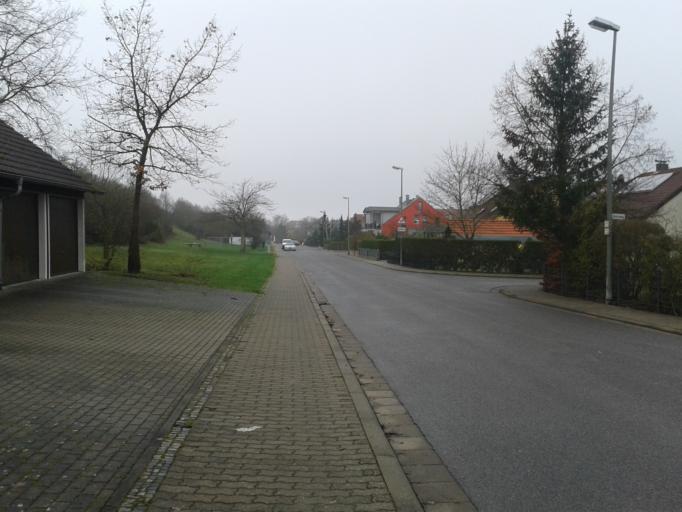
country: DE
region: Bavaria
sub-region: Upper Franconia
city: Hallstadt
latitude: 49.9225
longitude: 10.8819
